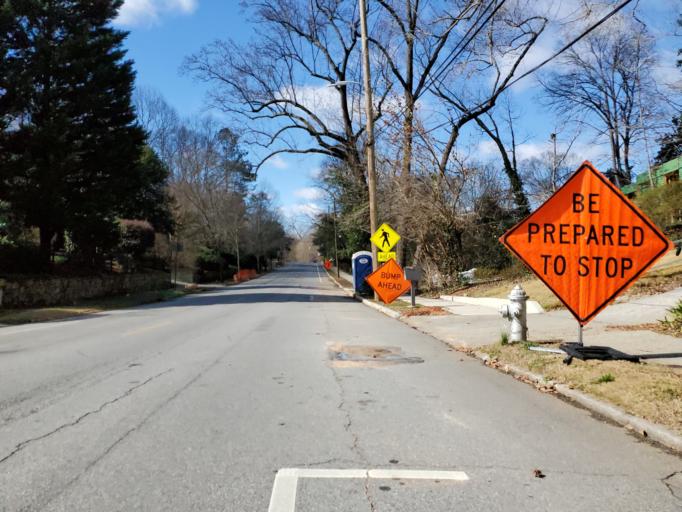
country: US
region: Georgia
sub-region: DeKalb County
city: Druid Hills
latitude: 33.7646
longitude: -84.3235
